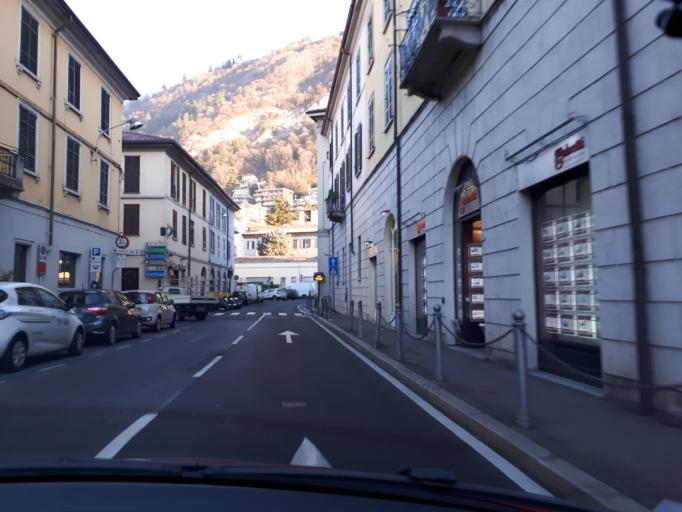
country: IT
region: Lombardy
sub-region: Provincia di Como
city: Como
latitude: 45.8144
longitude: 9.0846
